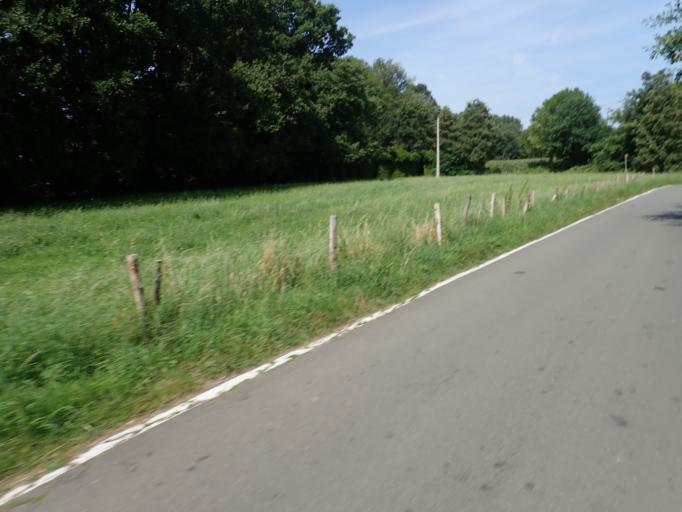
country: BE
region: Flanders
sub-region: Provincie Antwerpen
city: Wommelgem
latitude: 51.2010
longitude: 4.5352
